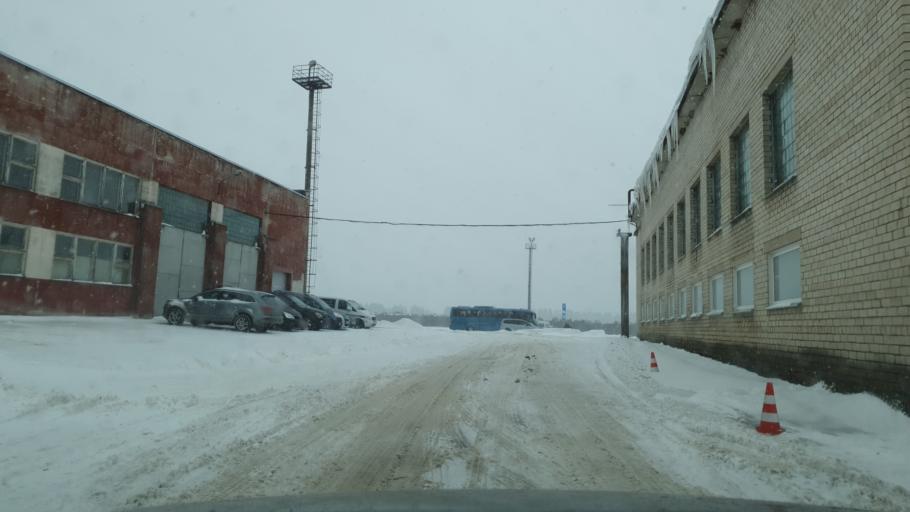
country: EE
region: Valgamaa
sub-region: Valga linn
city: Valga
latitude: 57.7930
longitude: 26.0414
